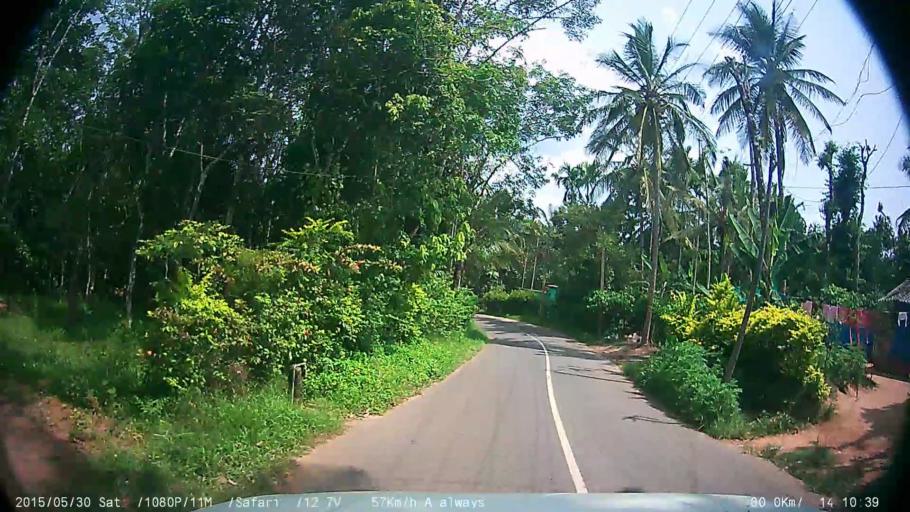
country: IN
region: Kerala
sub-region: Wayanad
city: Panamaram
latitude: 11.7975
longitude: 76.0524
